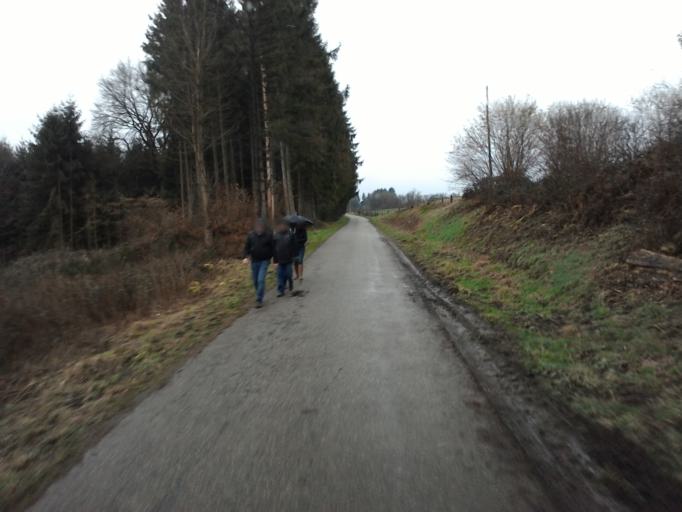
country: FR
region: Champagne-Ardenne
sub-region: Departement des Ardennes
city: Fromelennes
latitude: 50.0306
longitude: 4.8550
